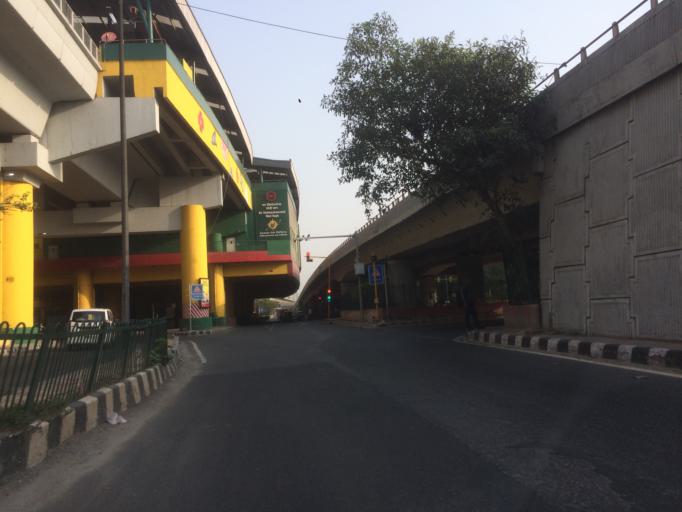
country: IN
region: NCT
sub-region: Central Delhi
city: Karol Bagh
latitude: 28.5778
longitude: 77.1763
